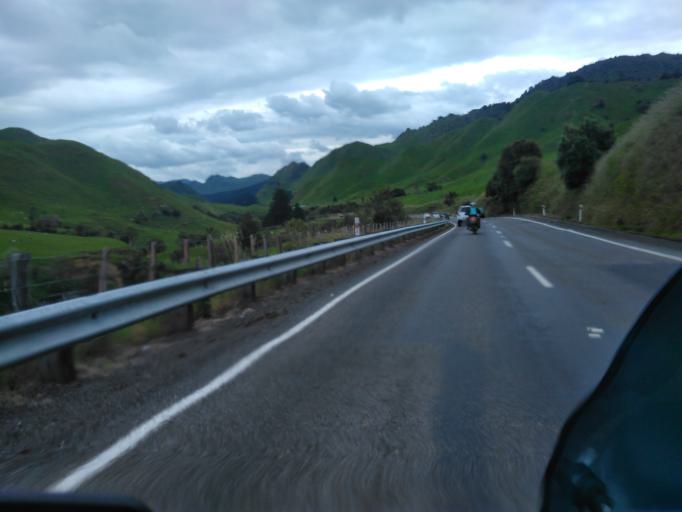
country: NZ
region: Bay of Plenty
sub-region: Opotiki District
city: Opotiki
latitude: -38.3627
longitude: 177.4624
